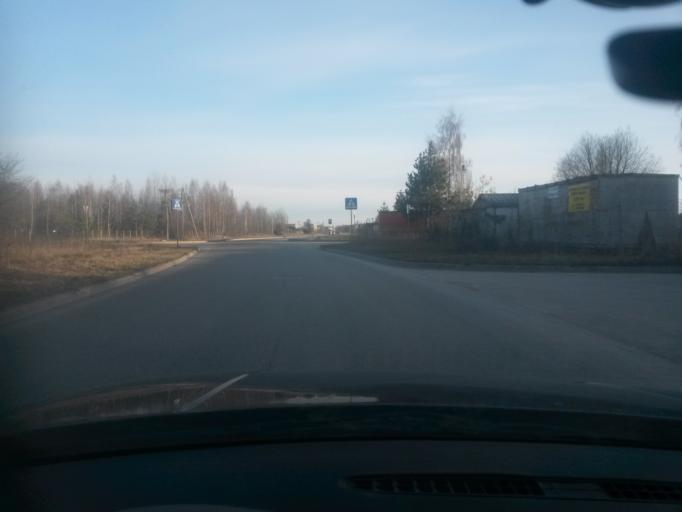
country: LV
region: Stopini
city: Ulbroka
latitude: 56.9057
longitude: 24.2466
